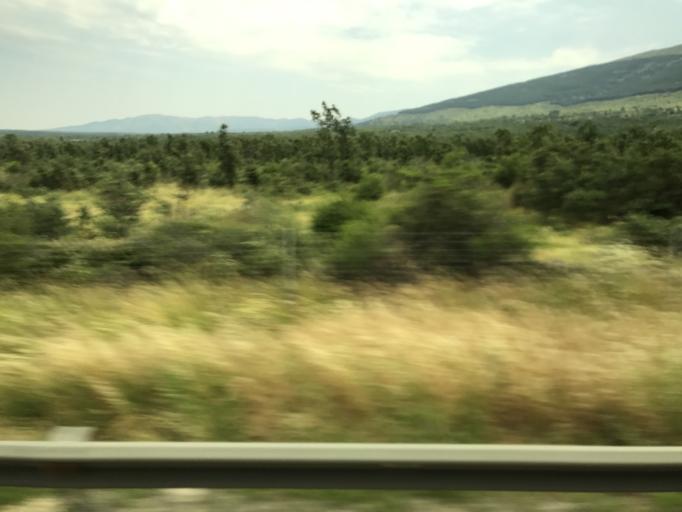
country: ES
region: Castille and Leon
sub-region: Provincia de Segovia
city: Cerezo de Abajo
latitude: 41.1806
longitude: -3.5836
